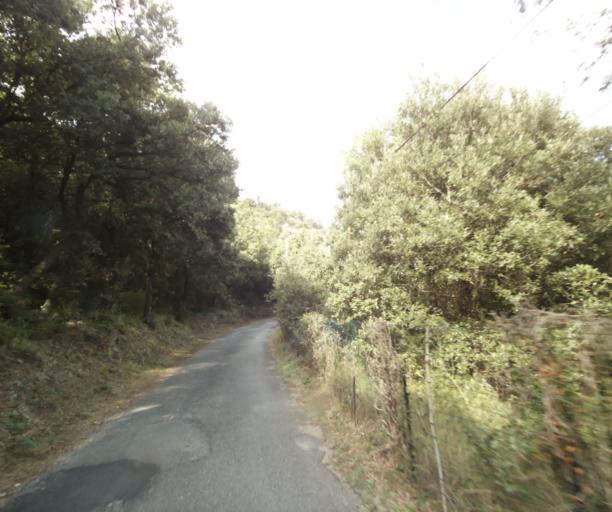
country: FR
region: Languedoc-Roussillon
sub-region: Departement des Pyrenees-Orientales
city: Sorede
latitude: 42.5196
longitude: 2.9892
